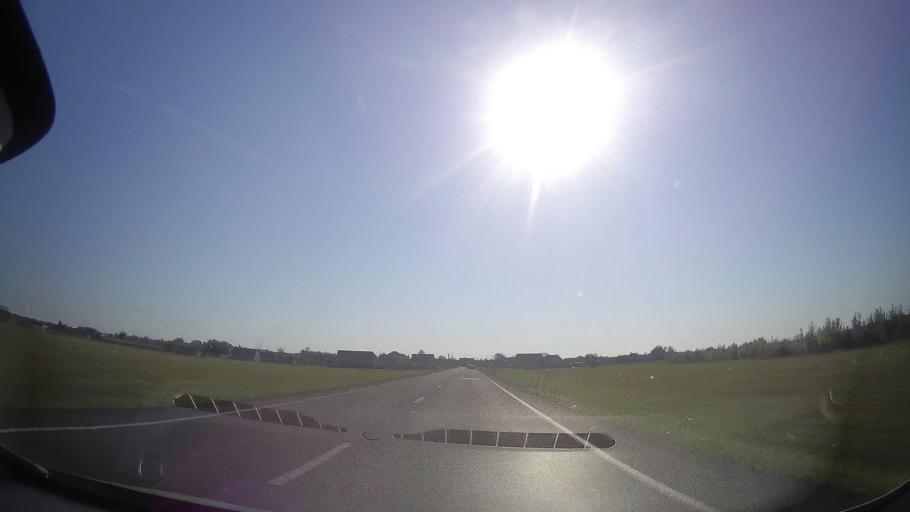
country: RO
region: Timis
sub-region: Comuna Topolovatu Mare
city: Topolovatu Mare
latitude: 45.7790
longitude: 21.6093
